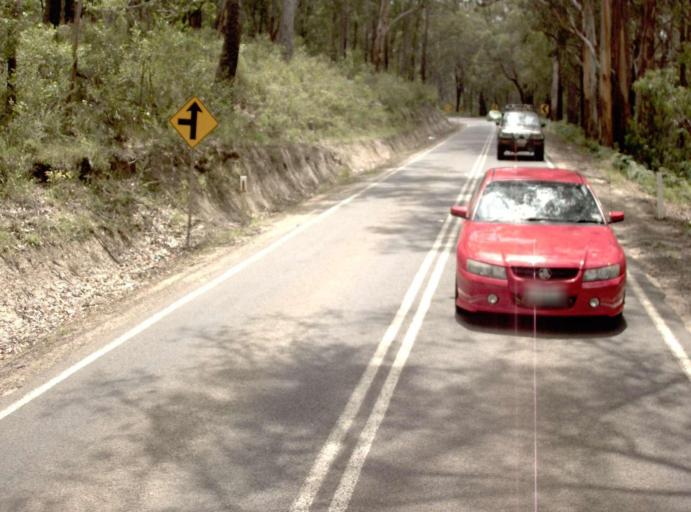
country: AU
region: Victoria
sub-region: Latrobe
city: Traralgon
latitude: -38.4206
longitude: 146.7476
